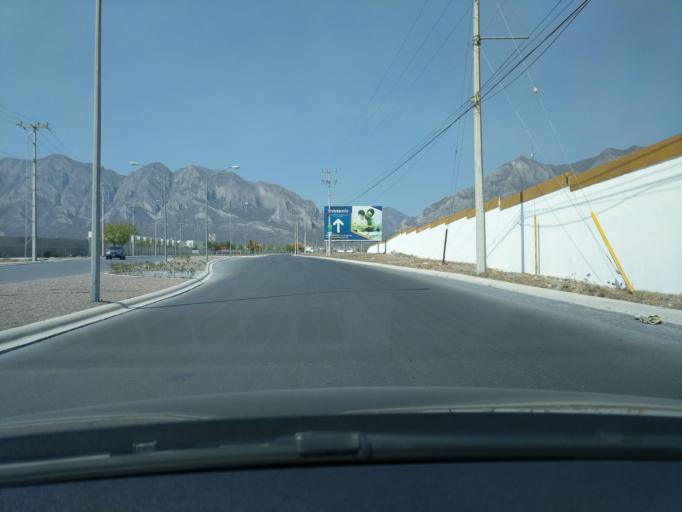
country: MX
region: Nuevo Leon
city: Garcia
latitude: 25.8088
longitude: -100.5376
